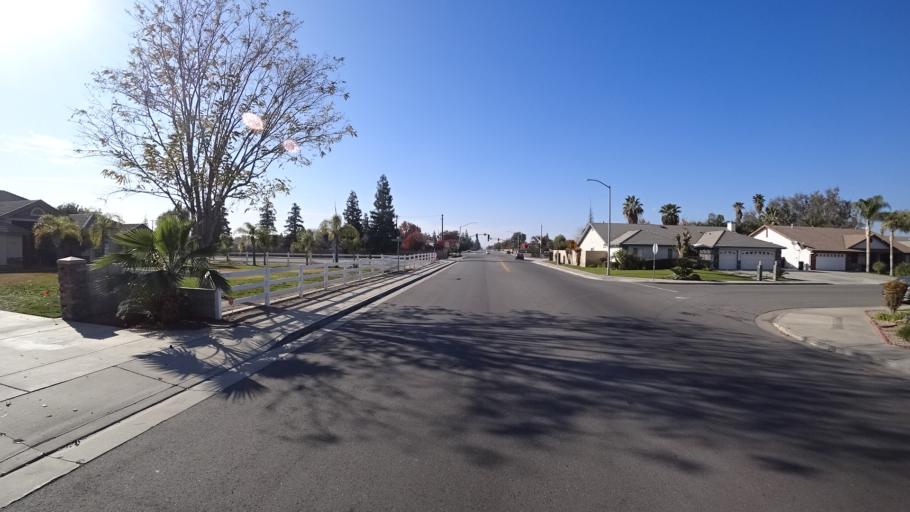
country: US
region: California
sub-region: Kern County
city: Greenfield
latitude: 35.2886
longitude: -119.0374
